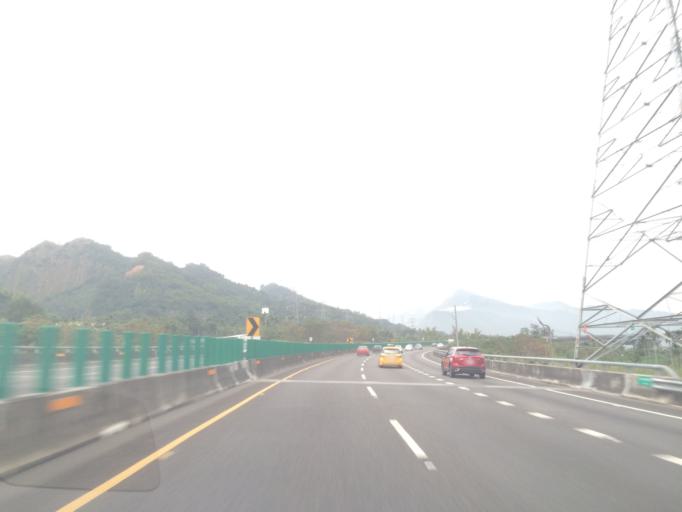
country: TW
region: Taiwan
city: Zhongxing New Village
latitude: 23.9951
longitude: 120.8012
